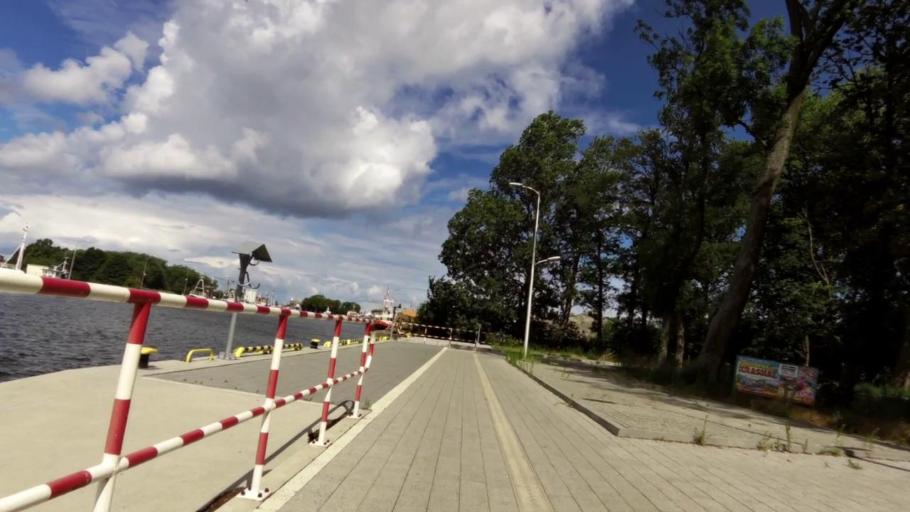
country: PL
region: West Pomeranian Voivodeship
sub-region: Powiat slawienski
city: Darlowo
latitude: 54.4346
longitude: 16.3891
